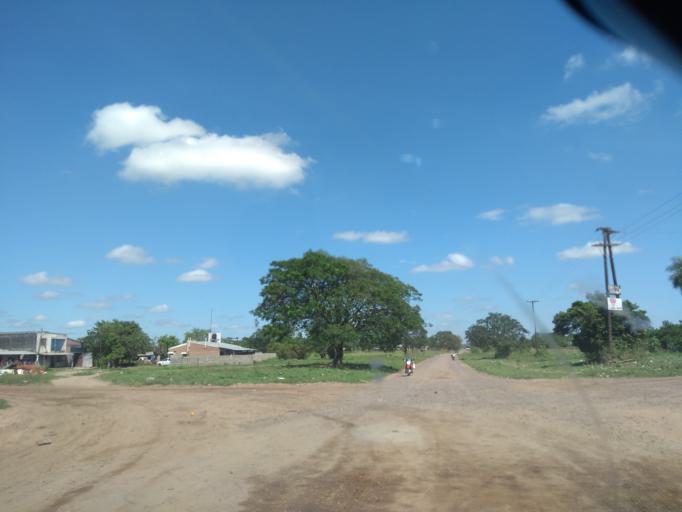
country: AR
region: Chaco
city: Fontana
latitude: -27.4058
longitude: -59.0376
